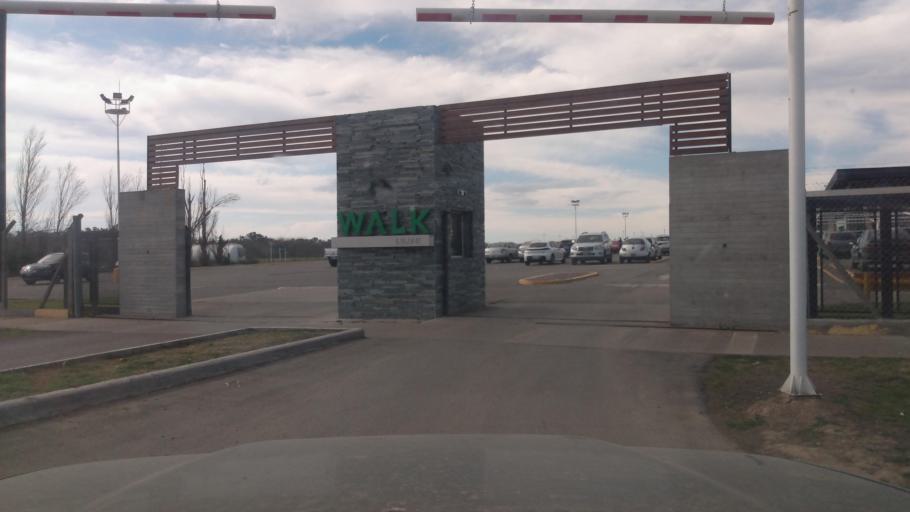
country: AR
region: Buenos Aires
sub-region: Partido de Lujan
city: Lujan
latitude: -34.5472
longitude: -59.1121
